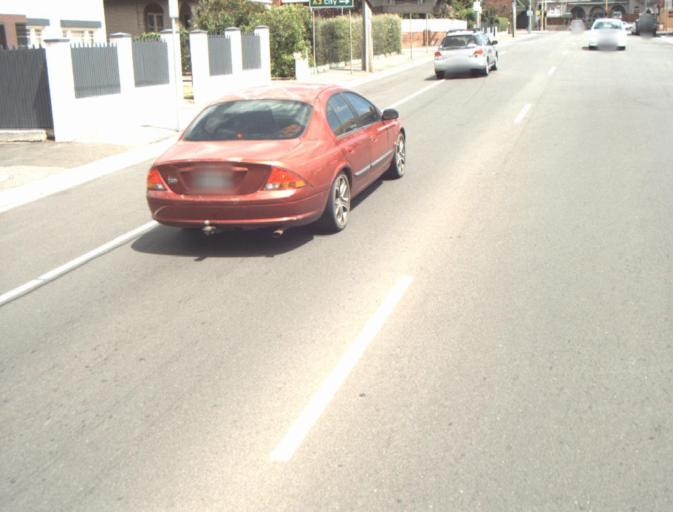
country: AU
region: Tasmania
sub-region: Launceston
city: Newstead
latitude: -41.4414
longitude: 147.1627
